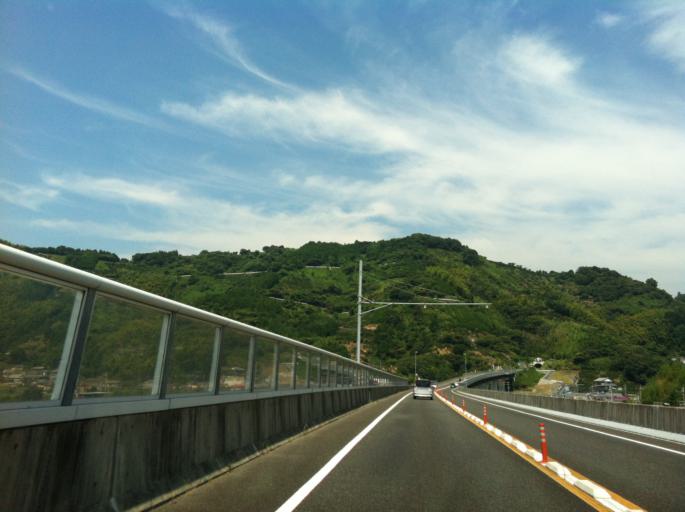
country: JP
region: Shizuoka
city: Shizuoka-shi
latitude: 35.0185
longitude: 138.3918
